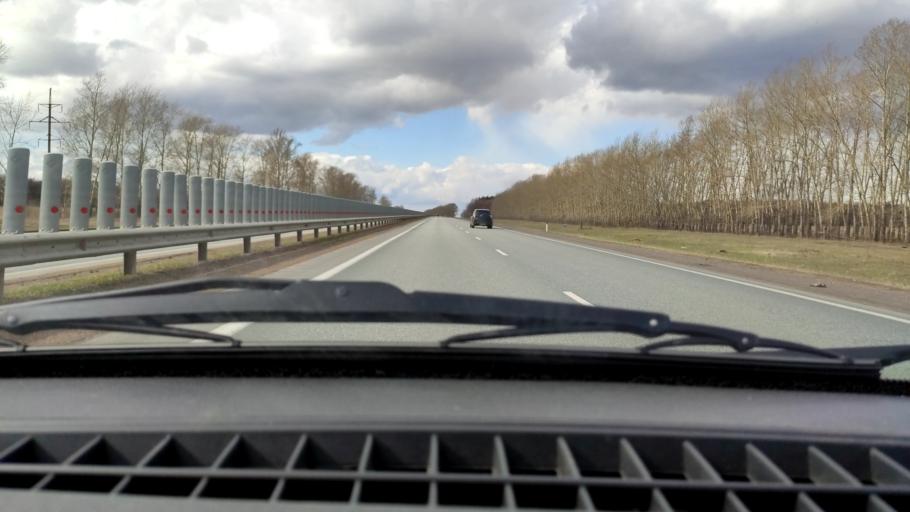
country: RU
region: Bashkortostan
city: Kushnarenkovo
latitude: 55.0409
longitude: 55.4518
